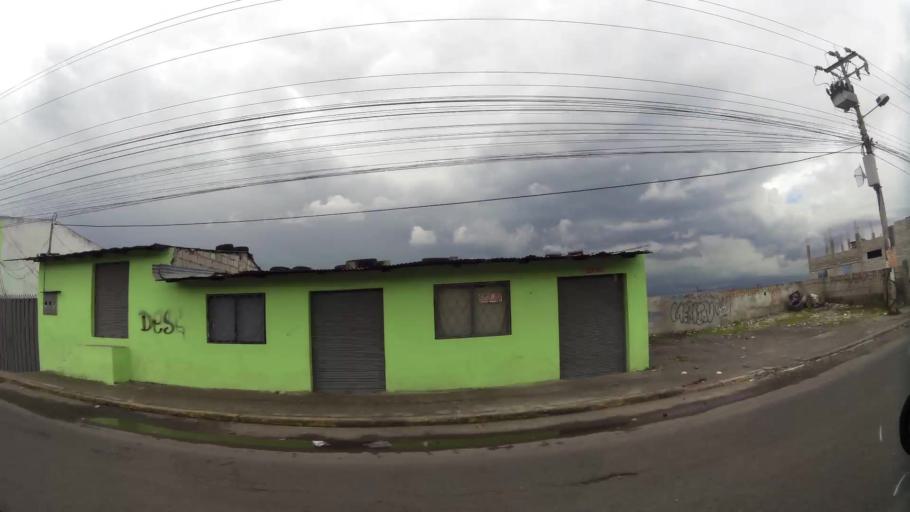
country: EC
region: Pichincha
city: Sangolqui
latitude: -0.3419
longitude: -78.5538
